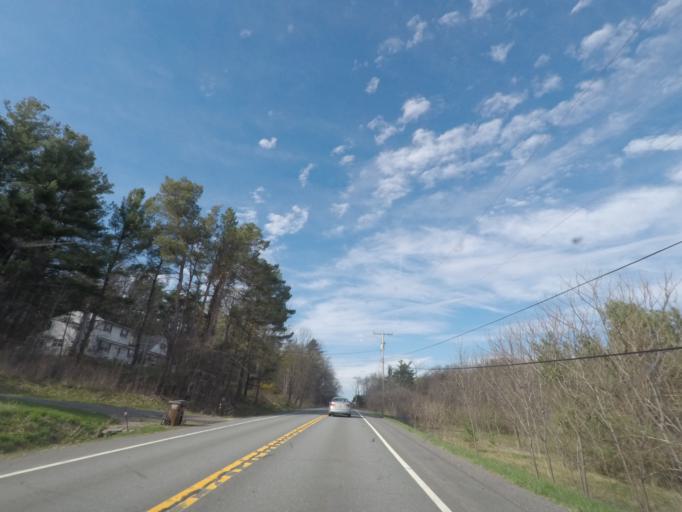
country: US
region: New York
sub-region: Albany County
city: Voorheesville
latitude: 42.6031
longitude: -73.9729
